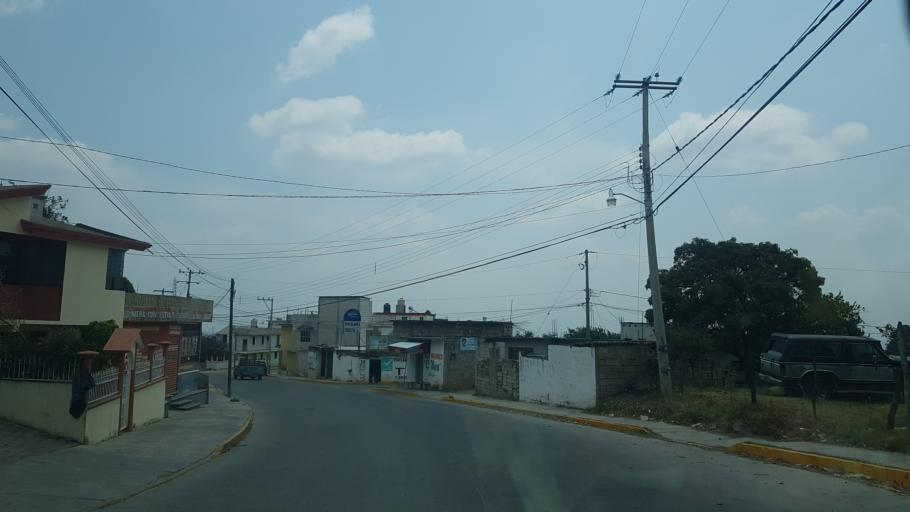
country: MX
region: Puebla
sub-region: Huejotzingo
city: San Juan Pancoac
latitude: 19.1384
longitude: -98.4403
